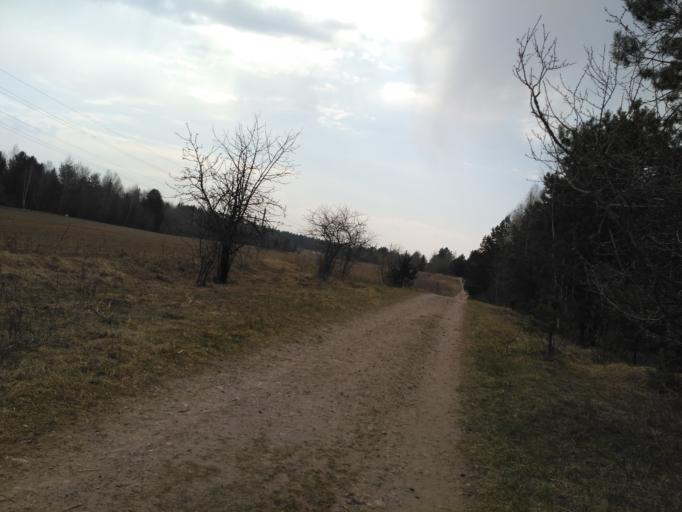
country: BY
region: Minsk
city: Zamostochcha
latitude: 53.8815
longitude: 27.9110
